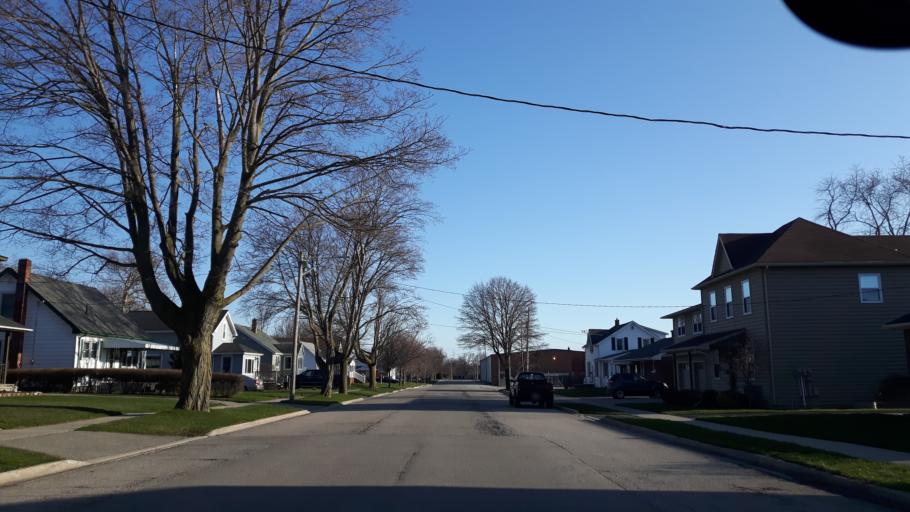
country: CA
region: Ontario
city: Goderich
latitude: 43.7387
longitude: -81.7138
